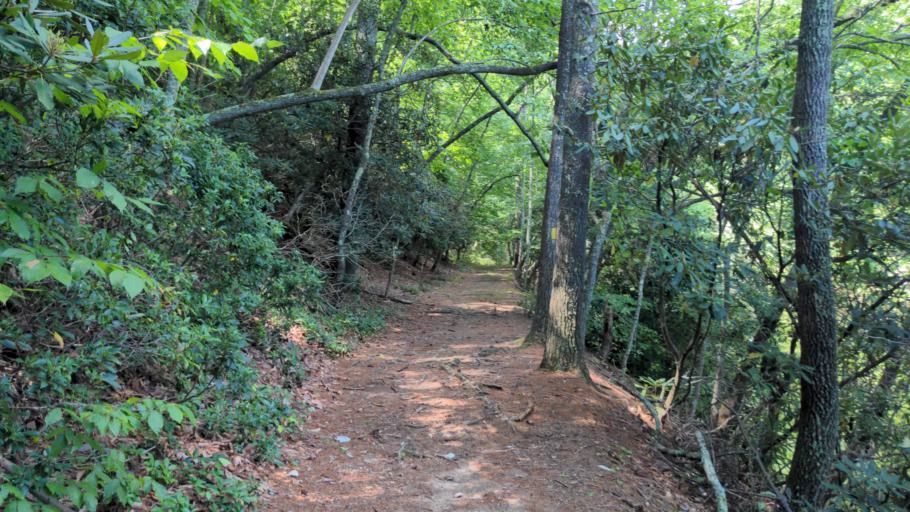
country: US
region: Virginia
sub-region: Henry County
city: Bassett
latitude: 36.7987
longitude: -80.1020
